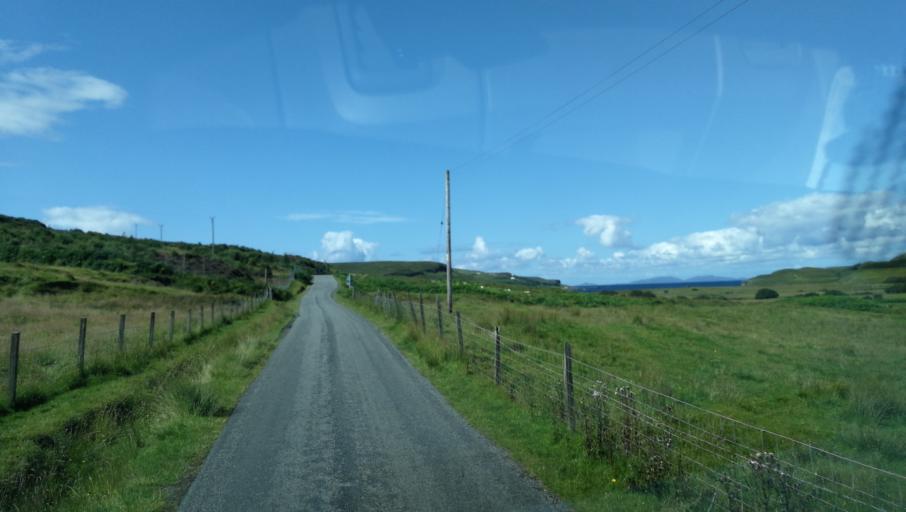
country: GB
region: Scotland
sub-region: Eilean Siar
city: Harris
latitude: 57.4486
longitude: -6.7093
